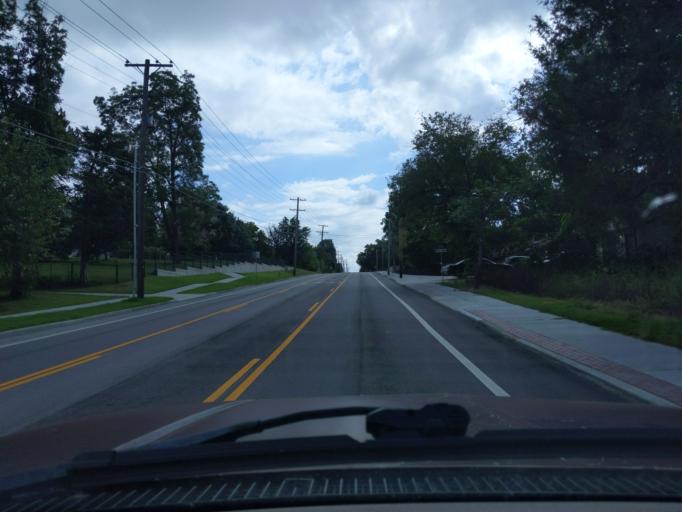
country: US
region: Oklahoma
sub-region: Tulsa County
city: Tulsa
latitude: 36.0997
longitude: -96.0116
